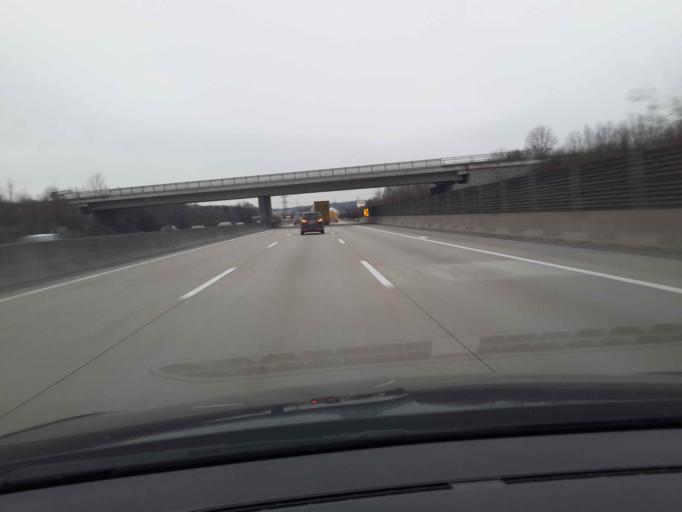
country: AT
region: Upper Austria
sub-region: Politischer Bezirk Linz-Land
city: Asten
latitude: 48.2176
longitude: 14.4090
